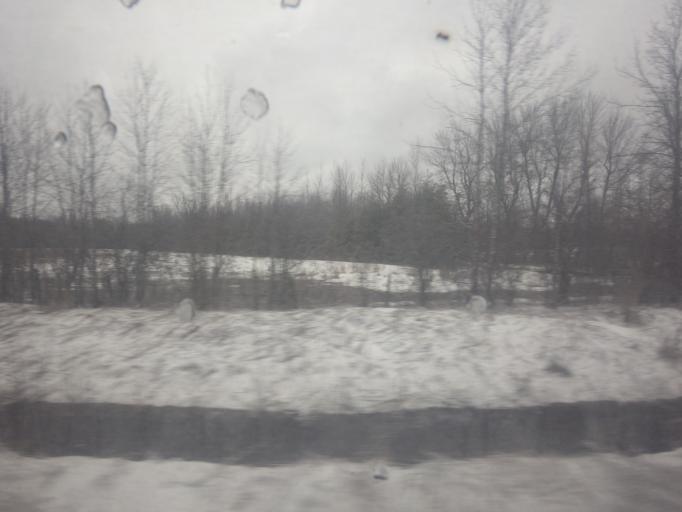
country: CA
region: Ontario
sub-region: Lanark County
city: Smiths Falls
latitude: 44.9318
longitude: -76.0268
